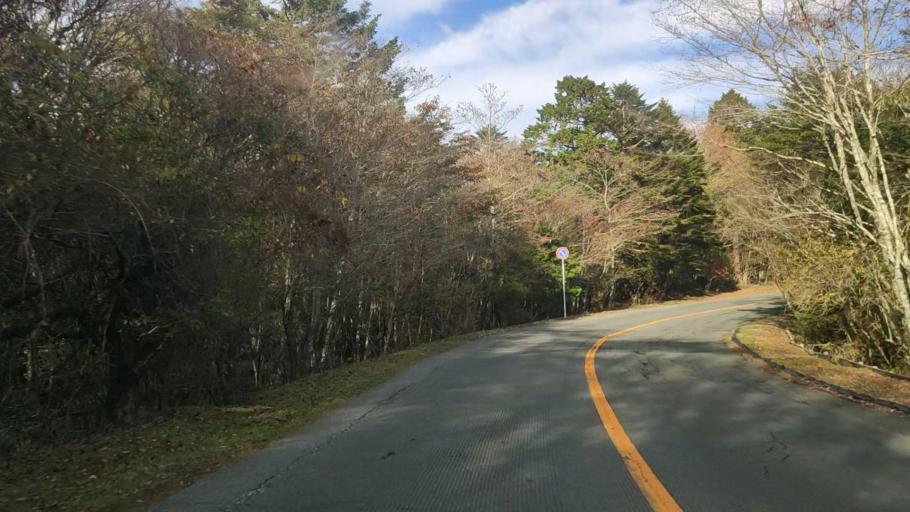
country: JP
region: Shizuoka
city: Fuji
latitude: 35.3046
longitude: 138.7609
